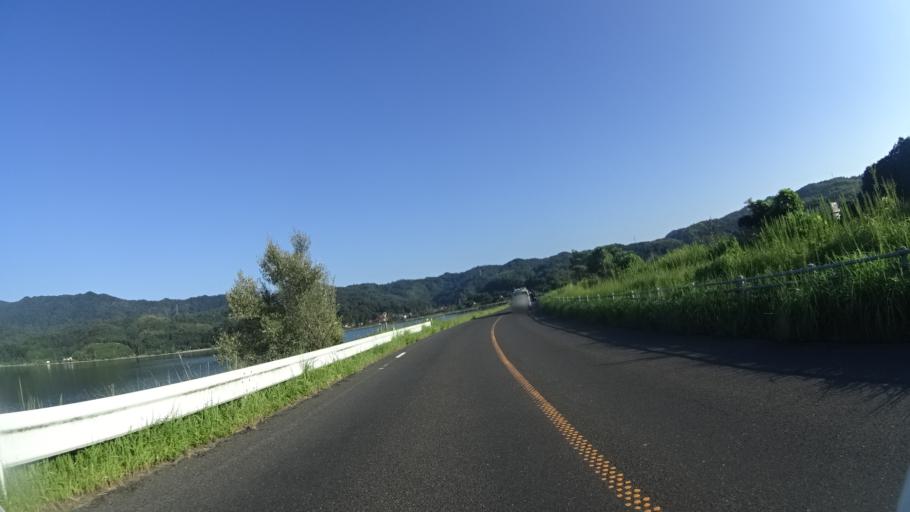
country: JP
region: Shimane
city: Sakaiminato
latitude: 35.5331
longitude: 133.1611
